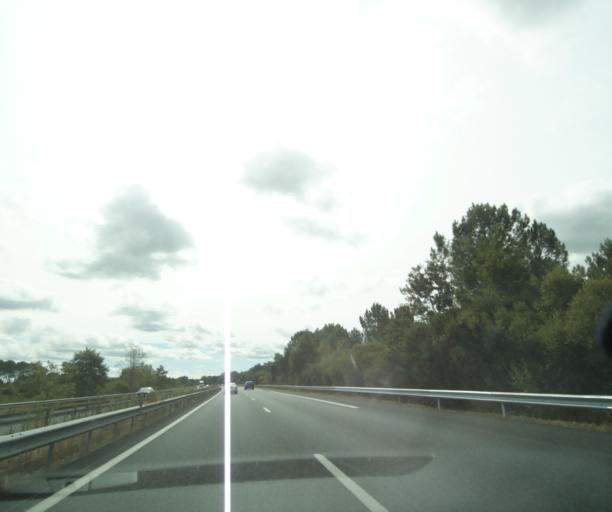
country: FR
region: Aquitaine
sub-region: Departement de la Gironde
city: Reignac
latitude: 45.2112
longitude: -0.5047
